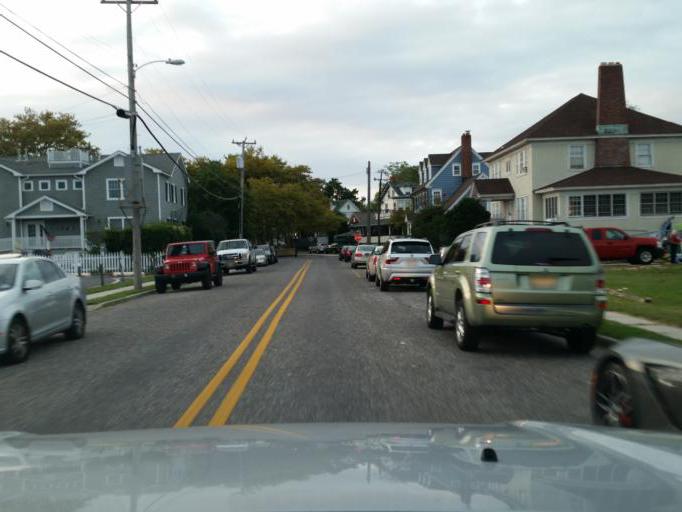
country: US
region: New Jersey
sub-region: Cape May County
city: Cape May
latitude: 38.9321
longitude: -74.9184
